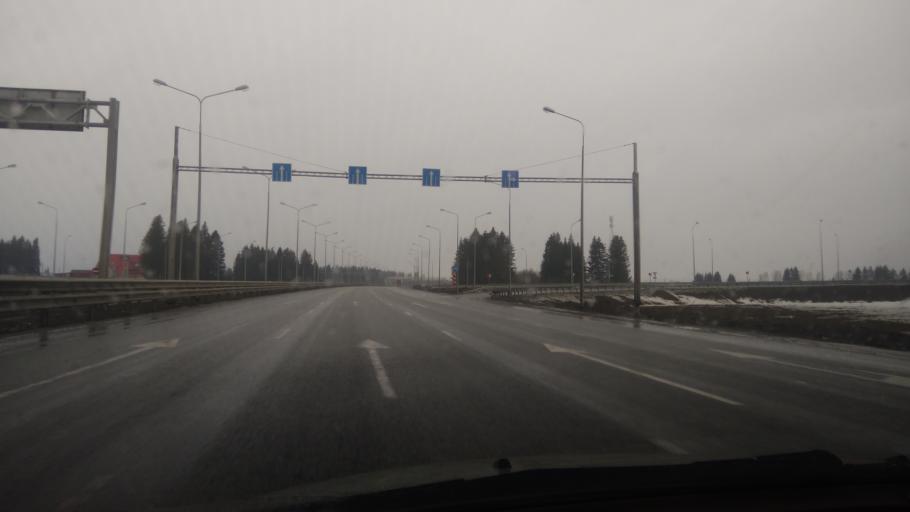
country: RU
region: Perm
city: Kukushtan
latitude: 57.6342
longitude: 56.4565
